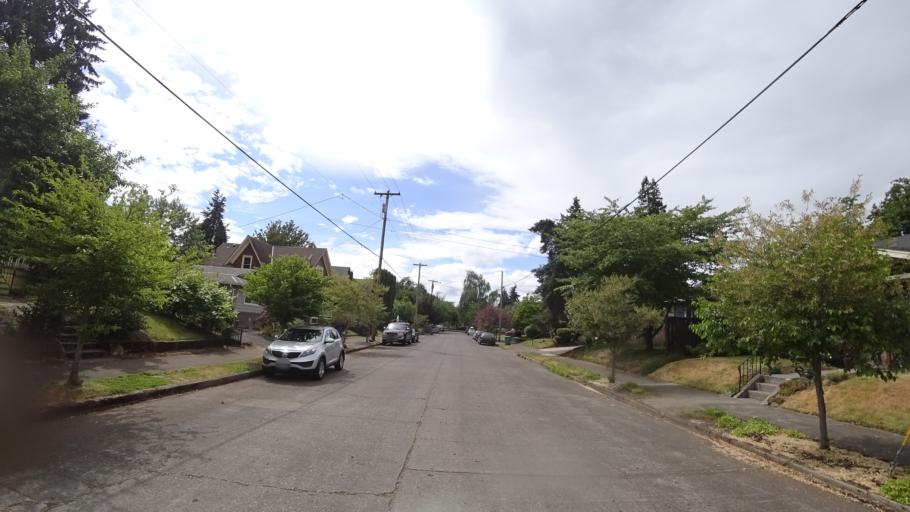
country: US
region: Oregon
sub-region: Washington County
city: West Haven
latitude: 45.5864
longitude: -122.7426
